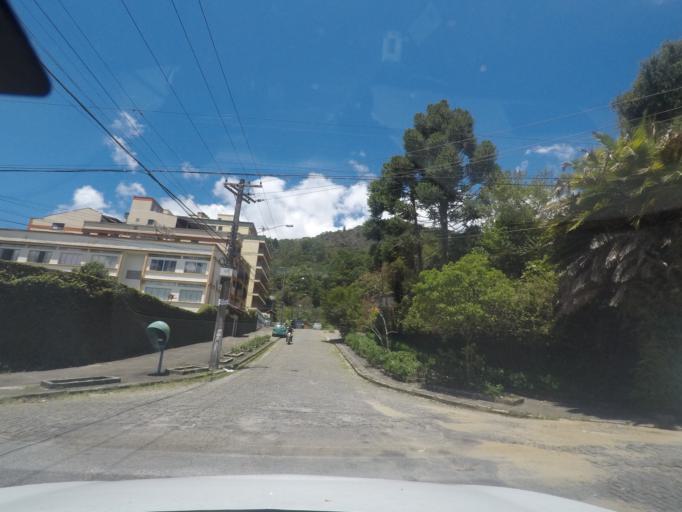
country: BR
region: Rio de Janeiro
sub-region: Teresopolis
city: Teresopolis
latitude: -22.4285
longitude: -42.9818
